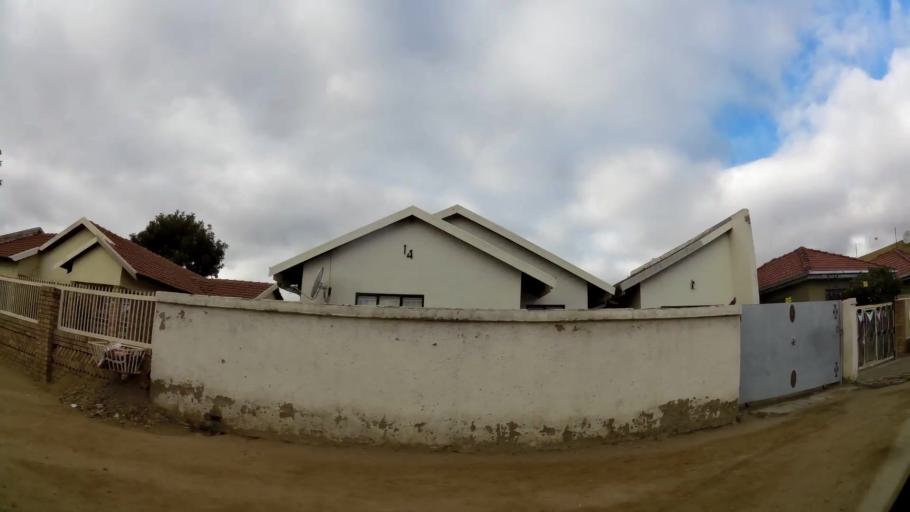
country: ZA
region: Limpopo
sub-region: Capricorn District Municipality
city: Polokwane
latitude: -23.9261
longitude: 29.4457
